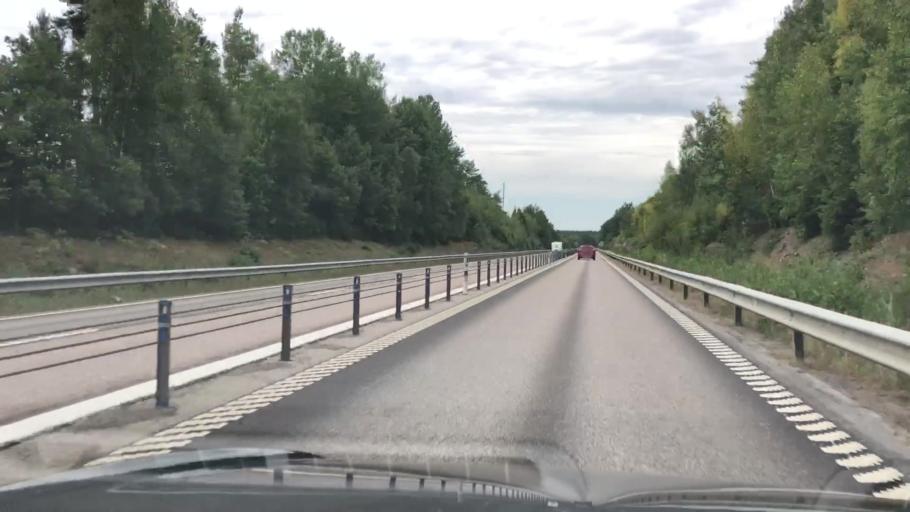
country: SE
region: Blekinge
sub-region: Karlshamns Kommun
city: Karlshamn
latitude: 56.1971
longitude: 14.9730
